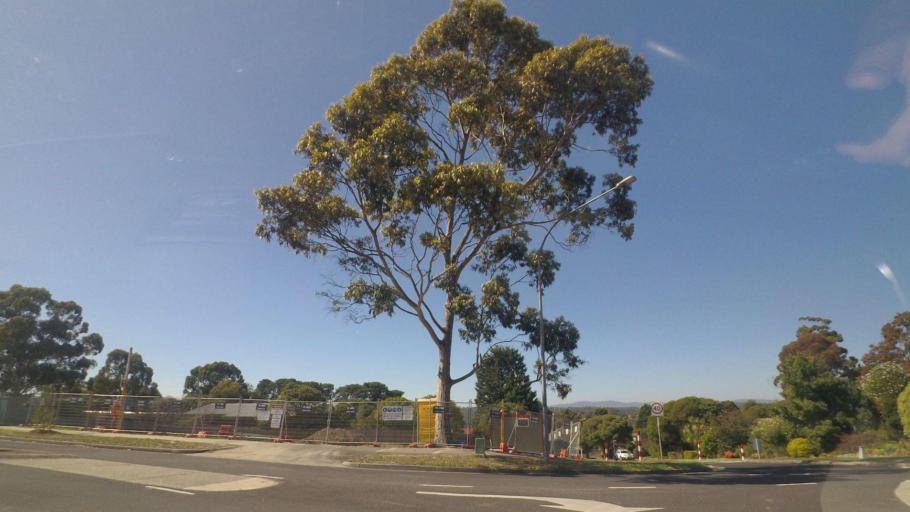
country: AU
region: Victoria
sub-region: Manningham
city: Donvale
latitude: -37.7752
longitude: 145.1745
